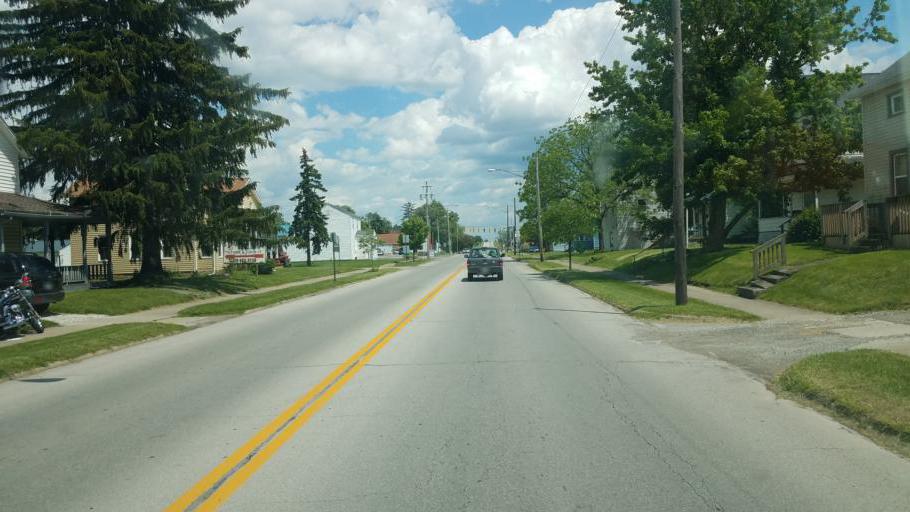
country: US
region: Ohio
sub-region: Crawford County
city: Crestline
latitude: 40.7875
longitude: -82.7283
